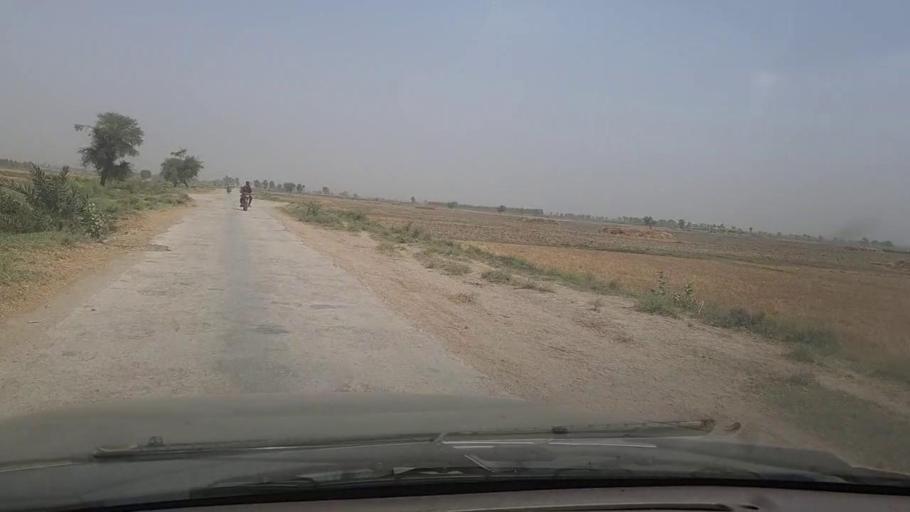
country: PK
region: Sindh
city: Madeji
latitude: 27.8102
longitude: 68.3979
